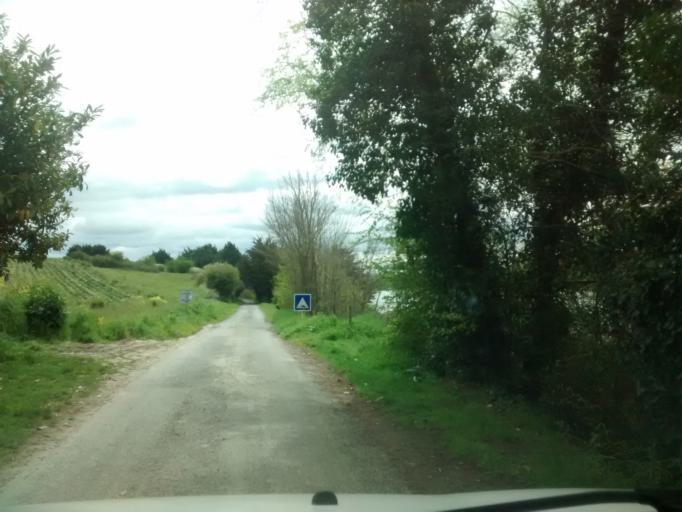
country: FR
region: Brittany
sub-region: Departement d'Ille-et-Vilaine
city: Saint-Jouan-des-Guerets
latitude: 48.5836
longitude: -1.9632
